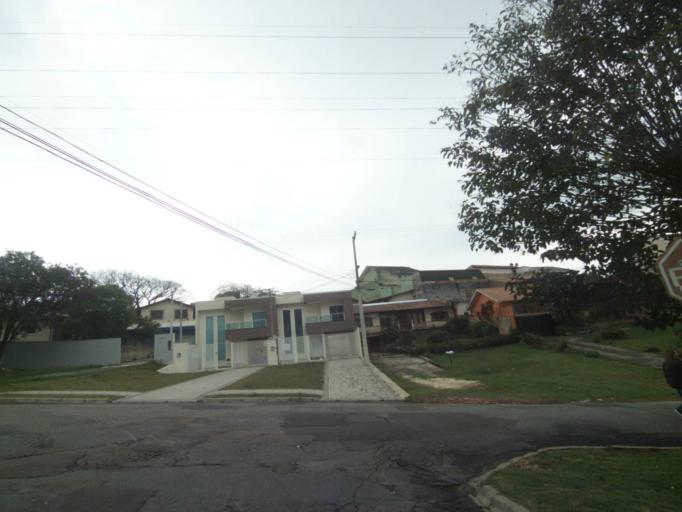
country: BR
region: Parana
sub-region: Curitiba
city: Curitiba
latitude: -25.4739
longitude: -49.3174
